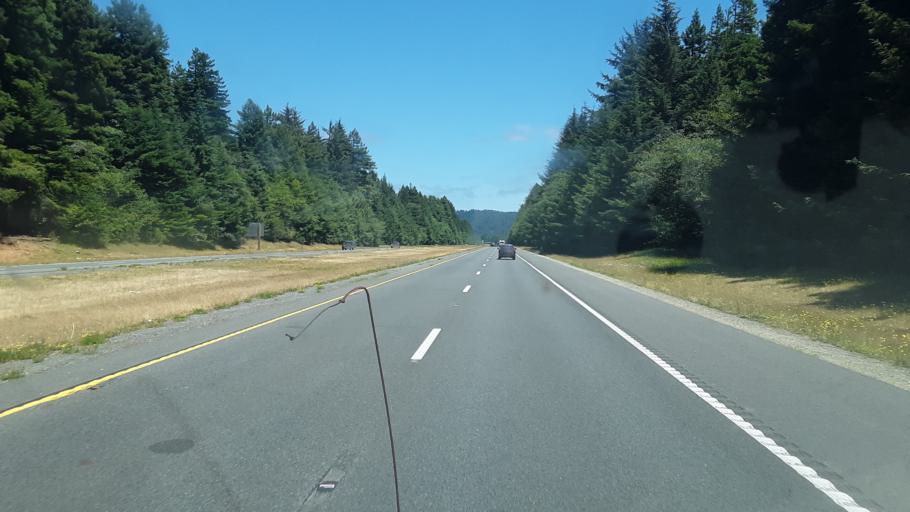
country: US
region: California
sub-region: Del Norte County
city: Bertsch-Oceanview
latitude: 41.7840
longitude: -124.1732
